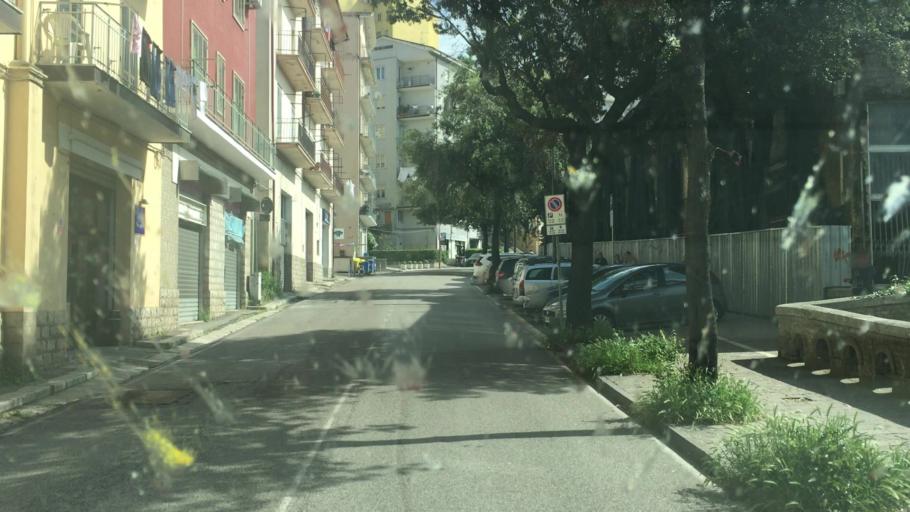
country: IT
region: Basilicate
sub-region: Provincia di Potenza
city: Potenza
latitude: 40.6414
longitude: 15.8046
